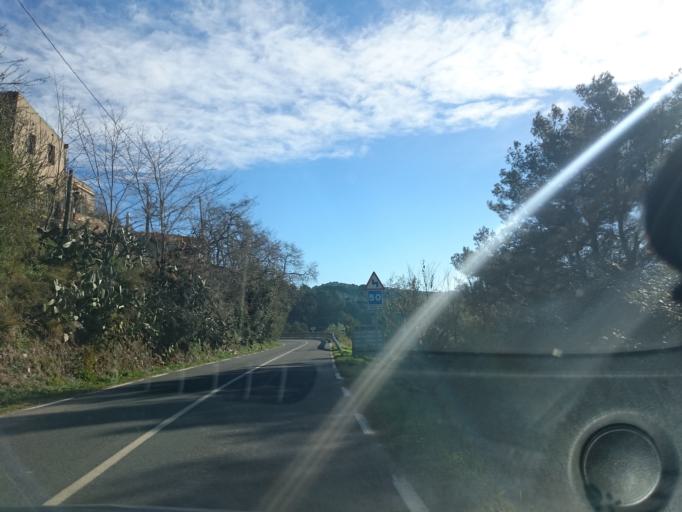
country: ES
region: Catalonia
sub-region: Provincia de Barcelona
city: Sant Just Desvern
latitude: 41.4082
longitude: 2.0891
